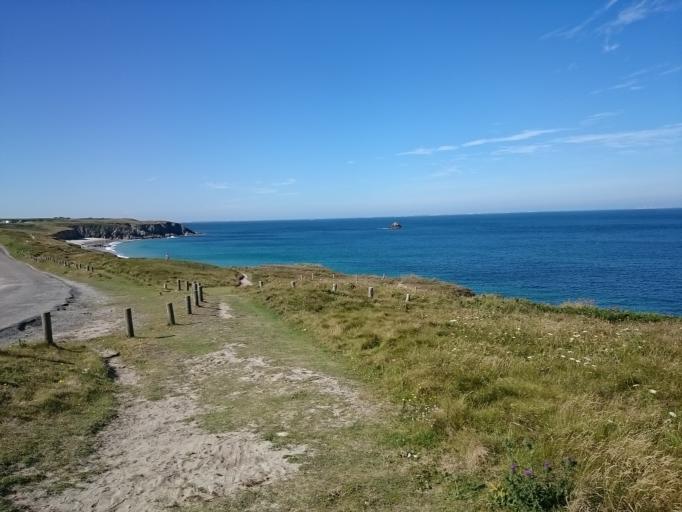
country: FR
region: Brittany
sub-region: Departement du Finistere
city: Lampaul-Plouarzel
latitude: 48.4288
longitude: -4.7857
